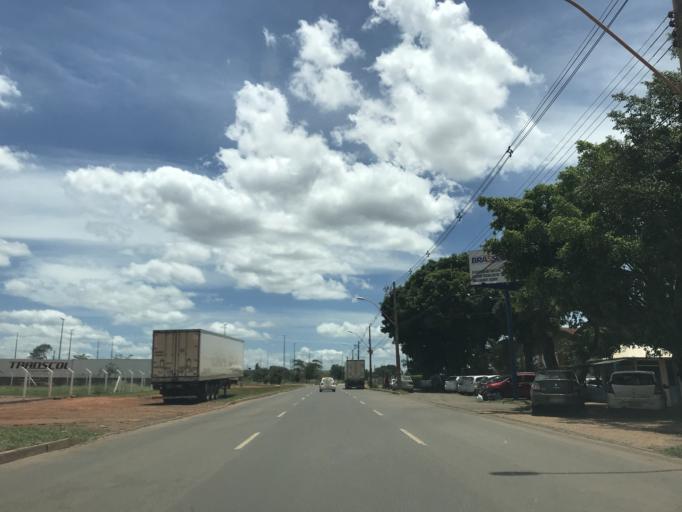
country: BR
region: Federal District
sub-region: Brasilia
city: Brasilia
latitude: -15.7945
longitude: -47.9762
